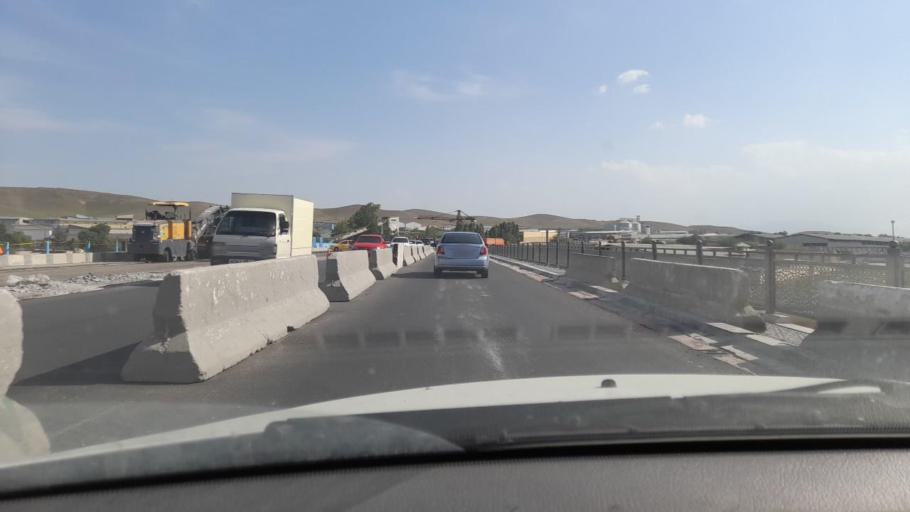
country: UZ
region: Samarqand
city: Samarqand
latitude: 39.6975
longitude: 67.0185
